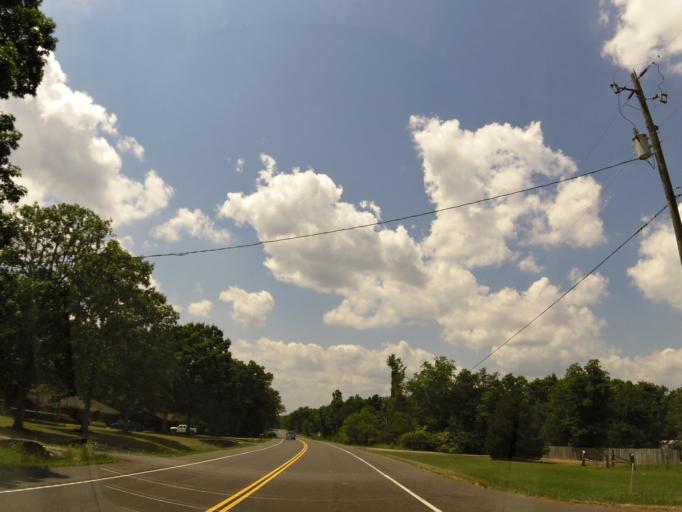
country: US
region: Tennessee
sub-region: Bledsoe County
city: Pikeville
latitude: 35.5678
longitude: -85.1017
